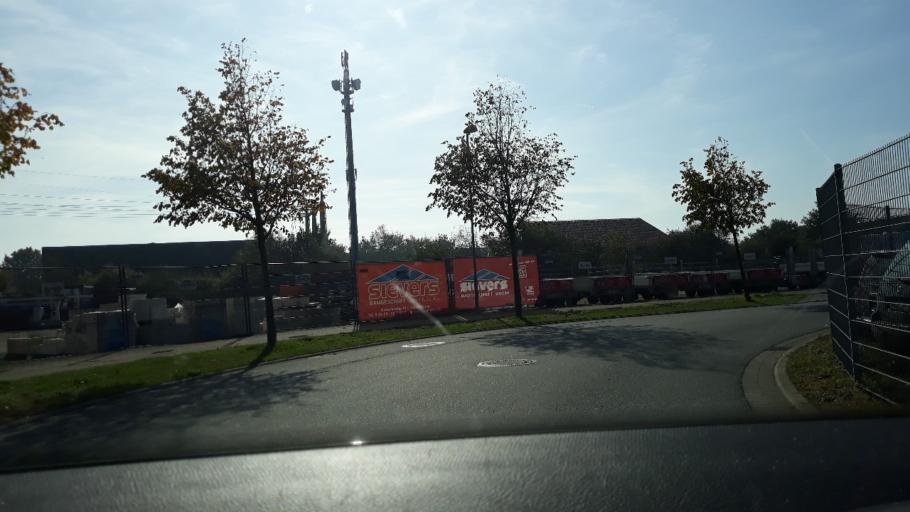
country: DE
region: Schleswig-Holstein
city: Kropp
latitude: 54.4175
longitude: 9.5274
